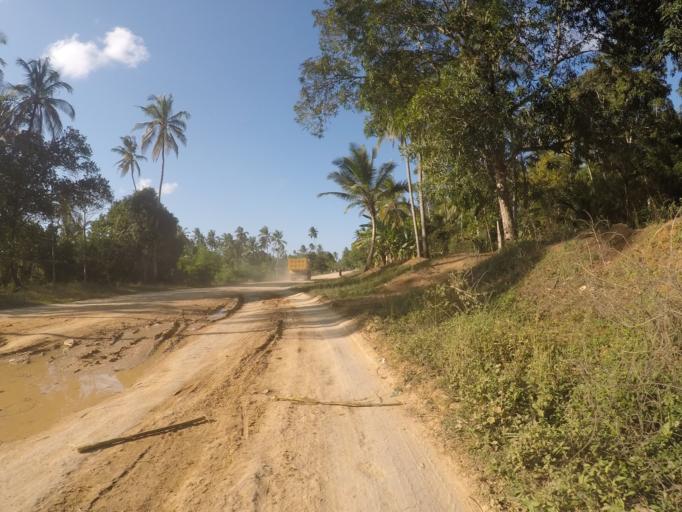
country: TZ
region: Zanzibar Central/South
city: Koani
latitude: -6.1746
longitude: 39.2842
